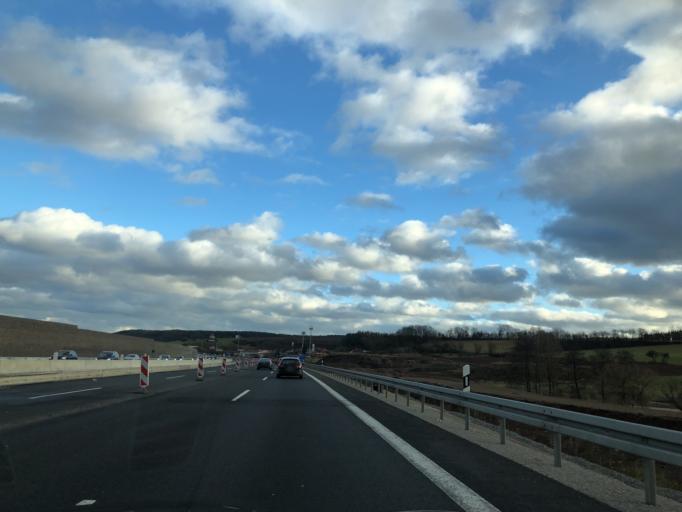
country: DE
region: Bavaria
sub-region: Regierungsbezirk Unterfranken
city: Geiselwind
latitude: 49.7736
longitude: 10.4603
